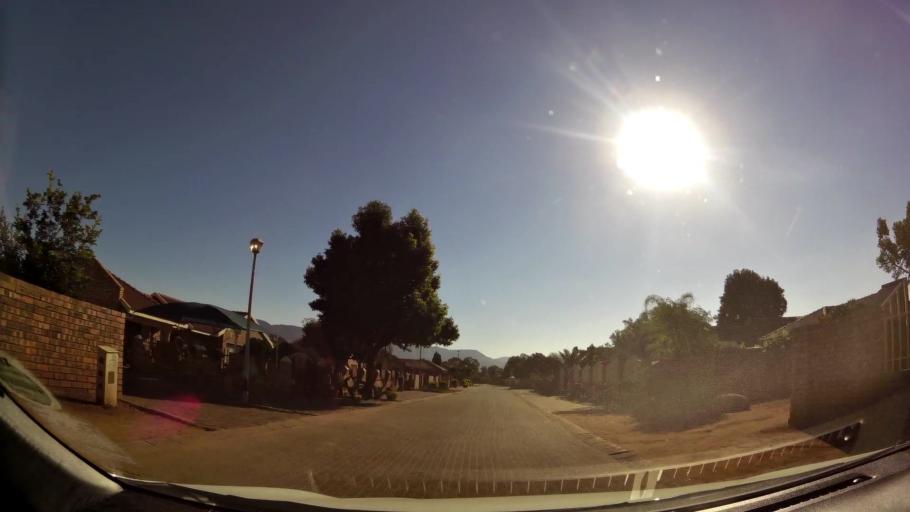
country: ZA
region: Limpopo
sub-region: Waterberg District Municipality
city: Mokopane
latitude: -24.1760
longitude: 28.9946
